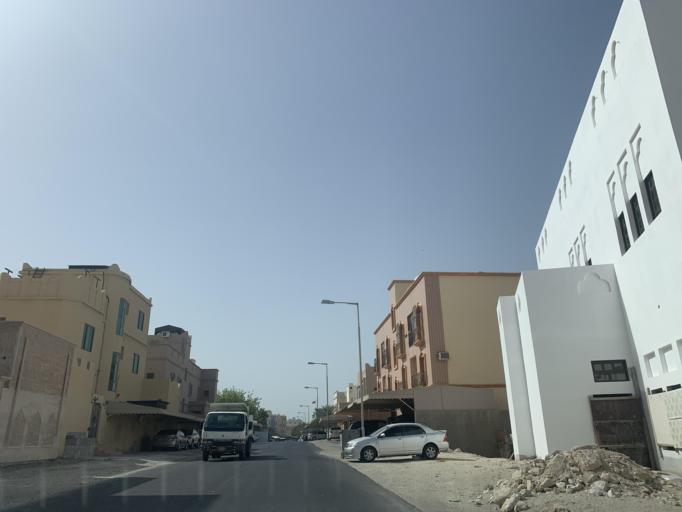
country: BH
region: Northern
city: Ar Rifa'
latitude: 26.1411
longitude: 50.5722
